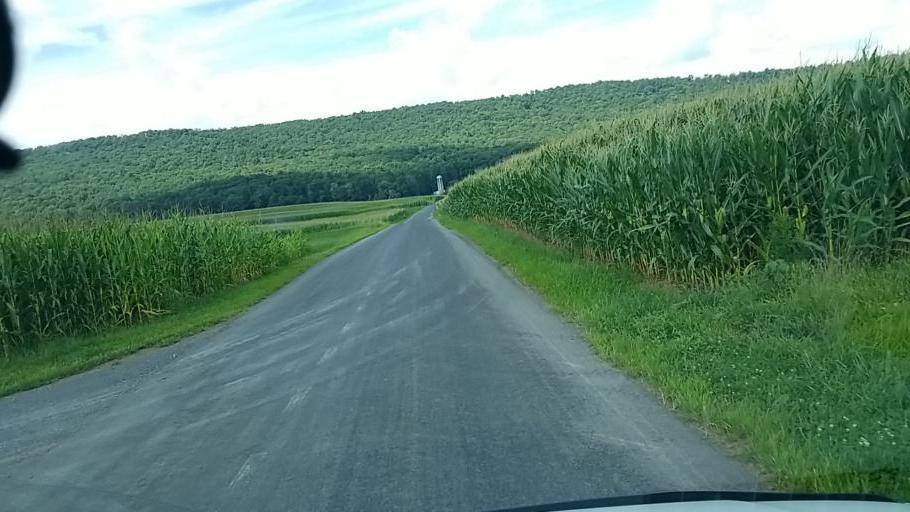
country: US
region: Pennsylvania
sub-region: Dauphin County
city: Elizabethville
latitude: 40.6049
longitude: -76.8522
